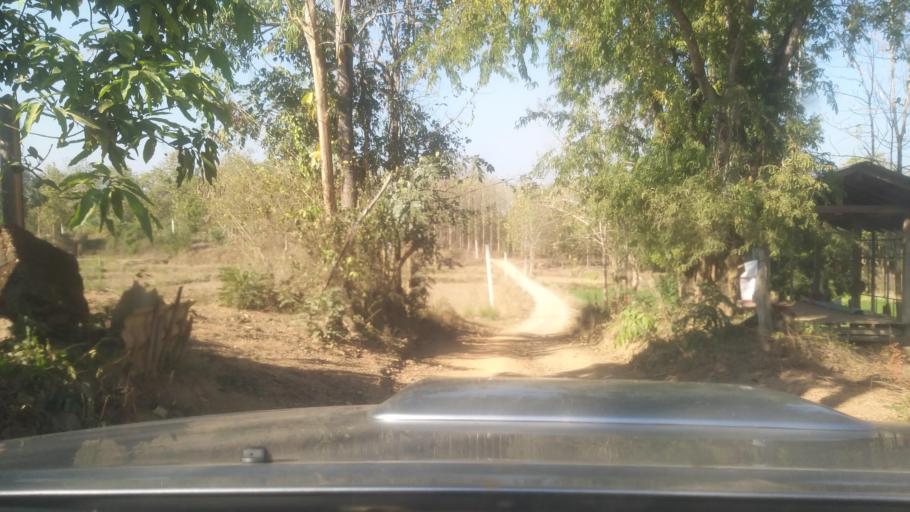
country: TH
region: Phrae
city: Phrae
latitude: 18.2711
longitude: 99.9794
